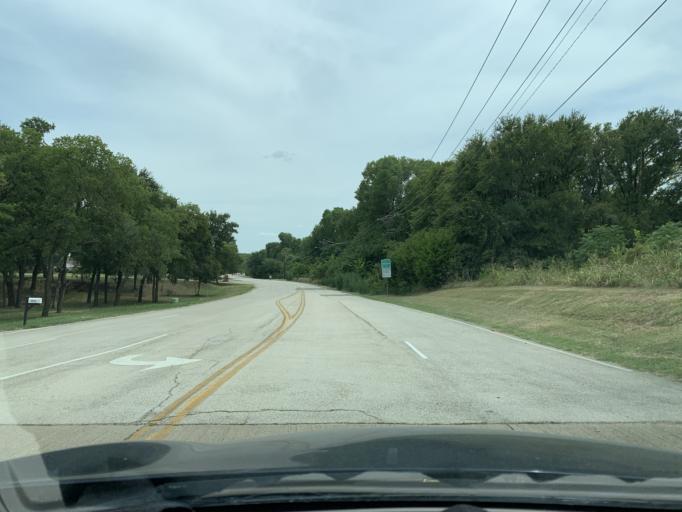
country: US
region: Texas
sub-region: Dallas County
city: Grand Prairie
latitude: 32.6690
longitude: -97.0310
